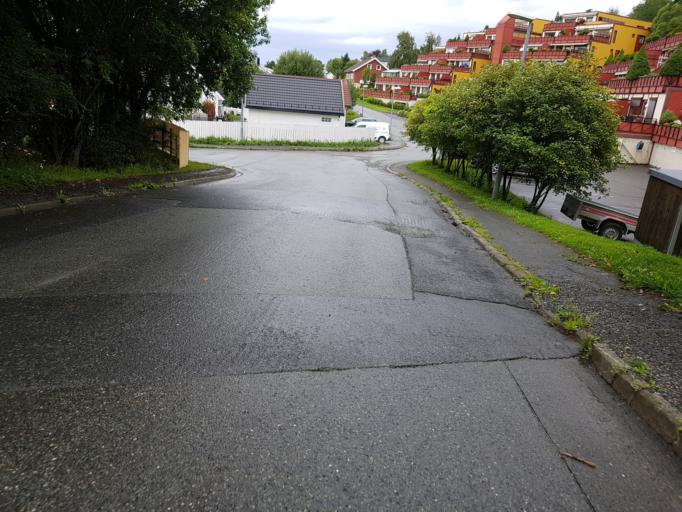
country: NO
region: Sor-Trondelag
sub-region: Trondheim
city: Trondheim
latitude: 63.3935
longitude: 10.4157
